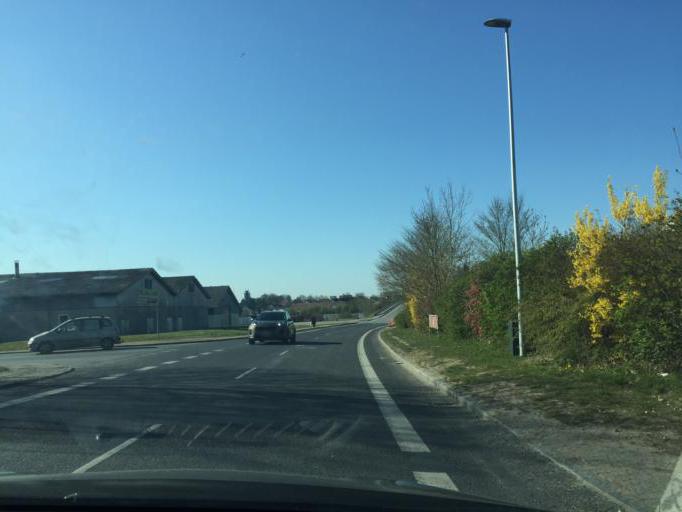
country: DK
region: South Denmark
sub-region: Faaborg-Midtfyn Kommune
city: Ringe
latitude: 55.2469
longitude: 10.4859
